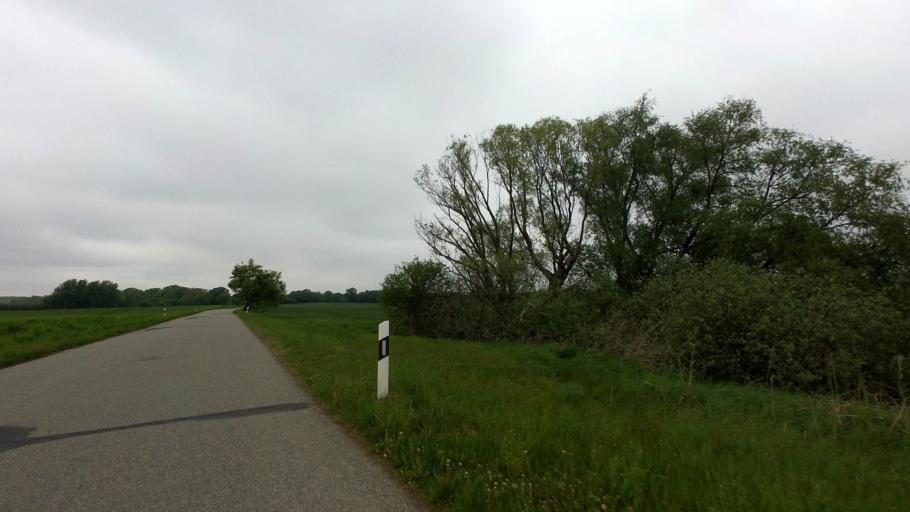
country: DE
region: Mecklenburg-Vorpommern
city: Mollenhagen
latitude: 53.6069
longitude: 12.9234
